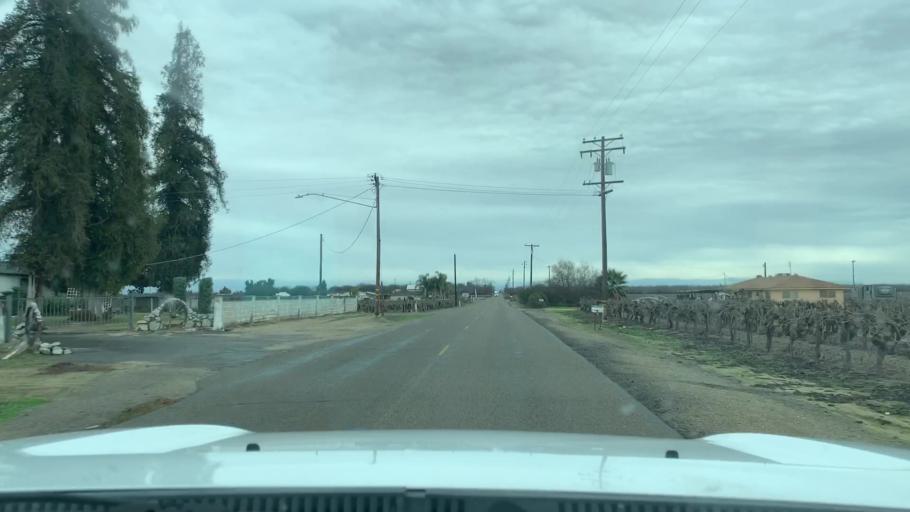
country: US
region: California
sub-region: Fresno County
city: Fowler
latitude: 36.5472
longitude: -119.6986
